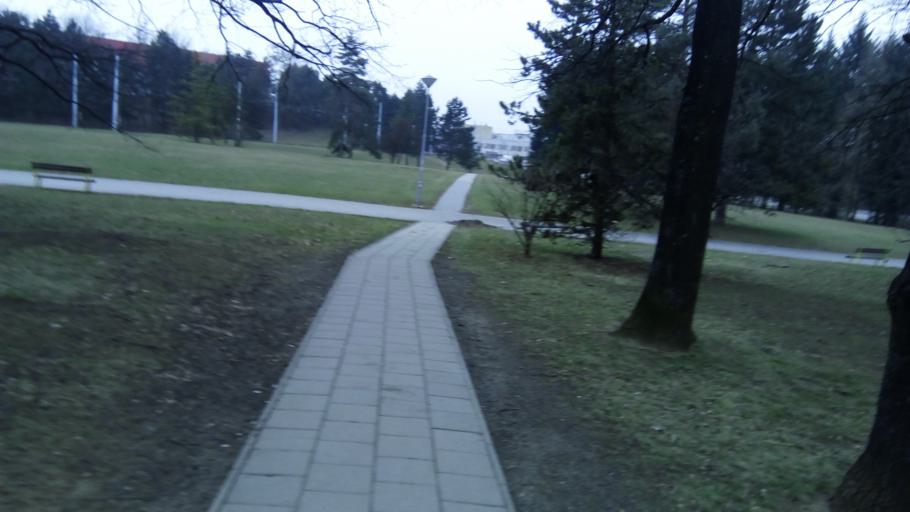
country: CZ
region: South Moravian
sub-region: Mesto Brno
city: Brno
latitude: 49.2254
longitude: 16.6215
